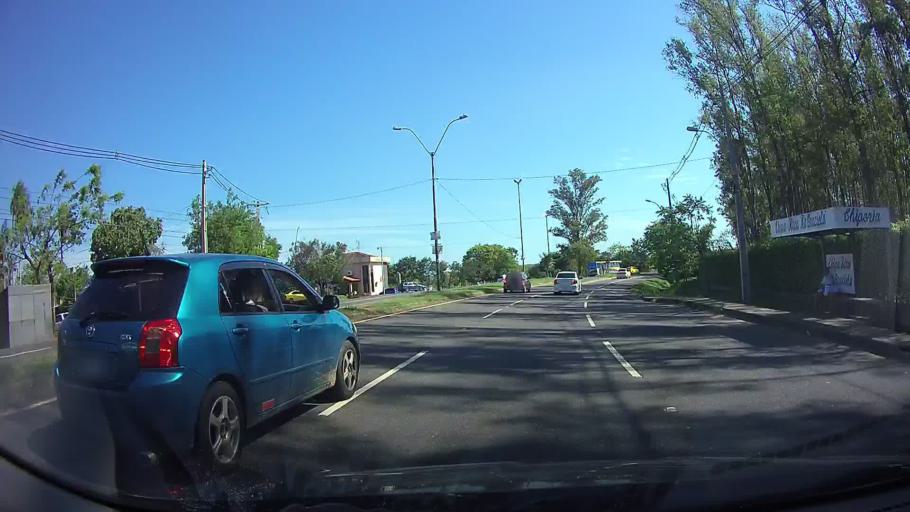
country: PY
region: Central
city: Ypacarai
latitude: -25.3825
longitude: -57.2628
